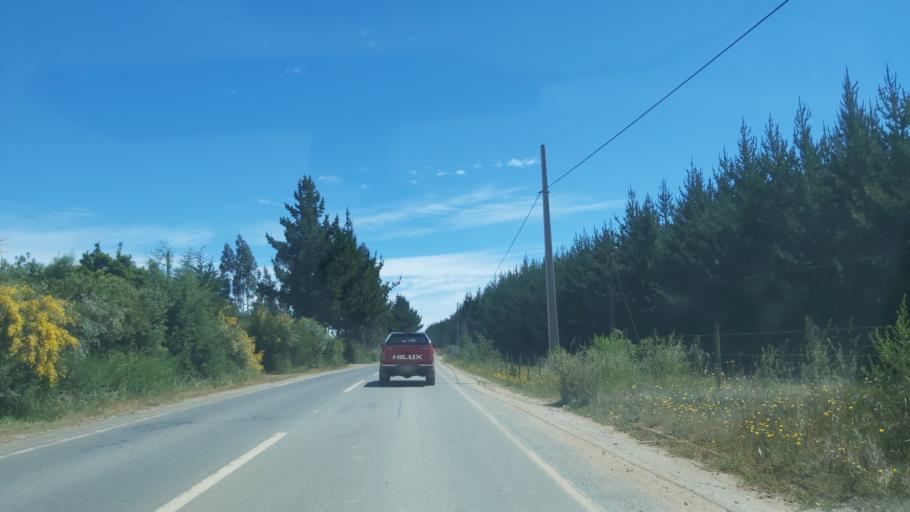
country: CL
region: Maule
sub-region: Provincia de Talca
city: Constitucion
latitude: -35.3928
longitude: -72.4264
